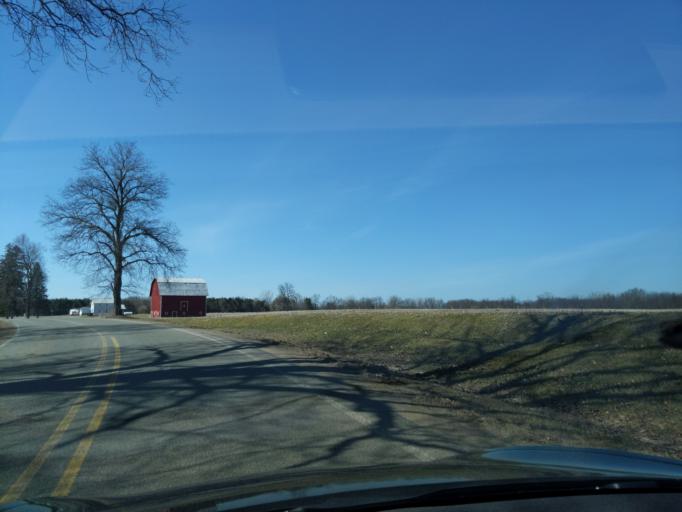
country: US
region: Michigan
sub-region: Ionia County
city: Lake Odessa
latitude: 42.7125
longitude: -85.0863
